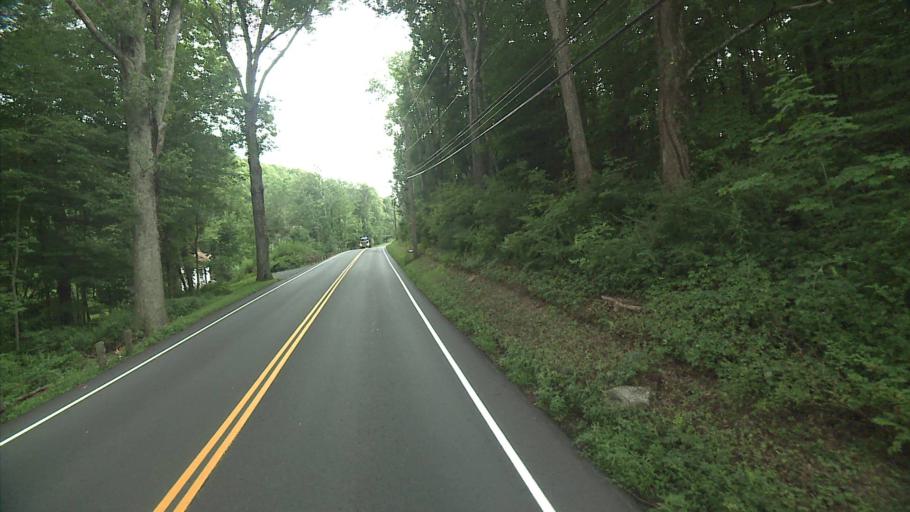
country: US
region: Connecticut
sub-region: New Haven County
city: Heritage Village
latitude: 41.5335
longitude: -73.2773
